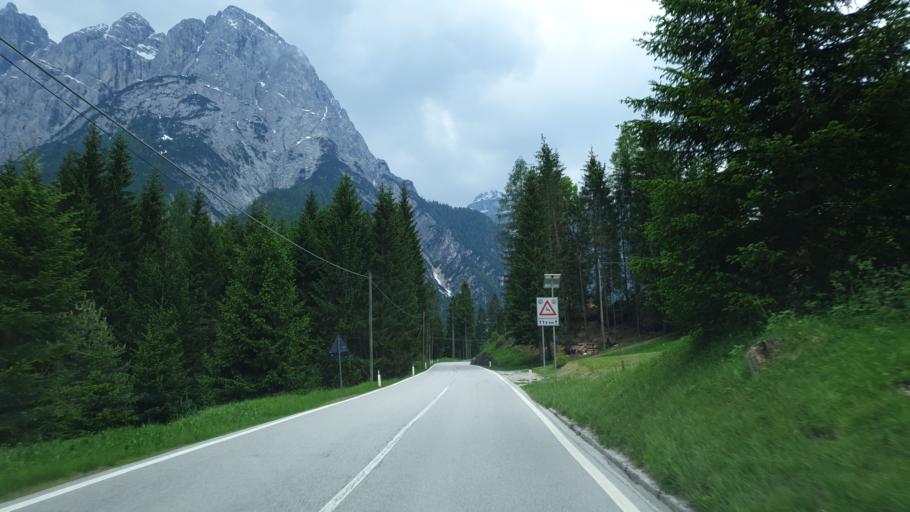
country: IT
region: Veneto
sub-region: Provincia di Belluno
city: Auronzo
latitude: 46.5552
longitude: 12.3385
